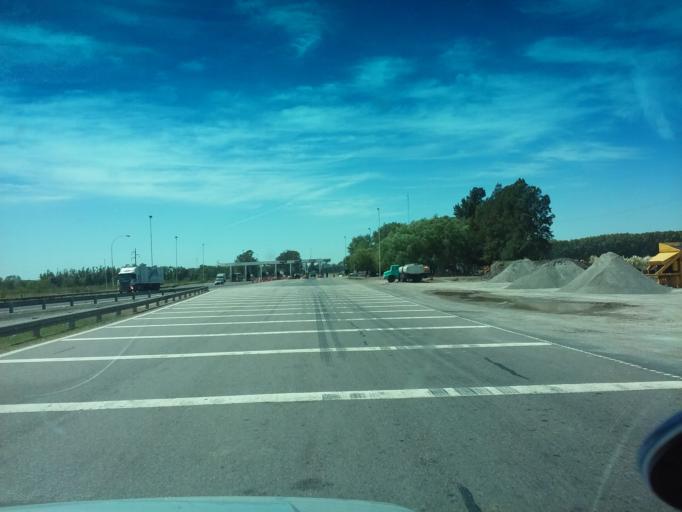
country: AR
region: Buenos Aires
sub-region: Partido de Mercedes
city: Mercedes
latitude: -34.6456
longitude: -59.2966
